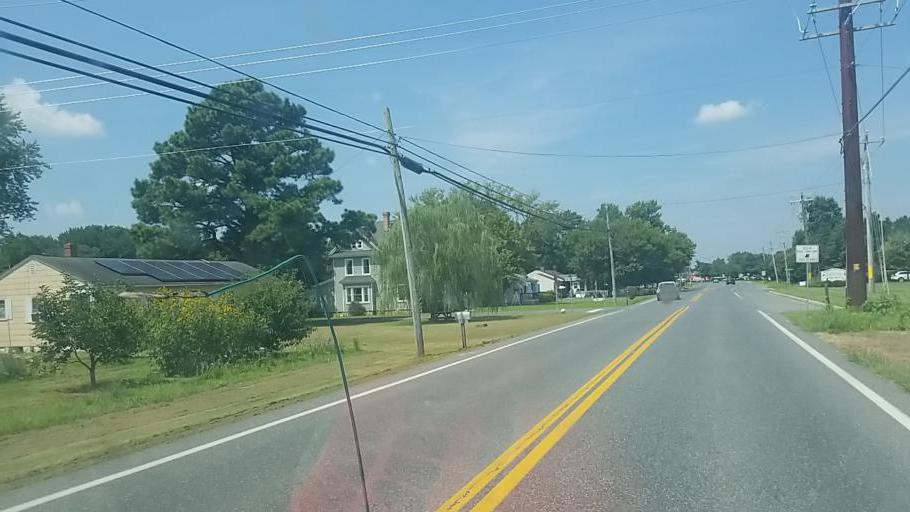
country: US
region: Maryland
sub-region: Wicomico County
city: Salisbury
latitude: 38.3647
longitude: -75.5621
